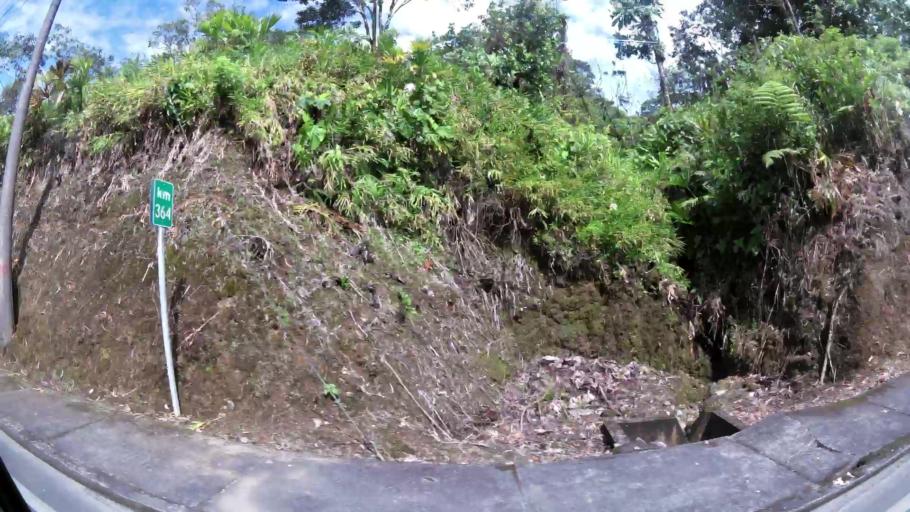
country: EC
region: Pastaza
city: Puyo
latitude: -1.5002
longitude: -78.0241
